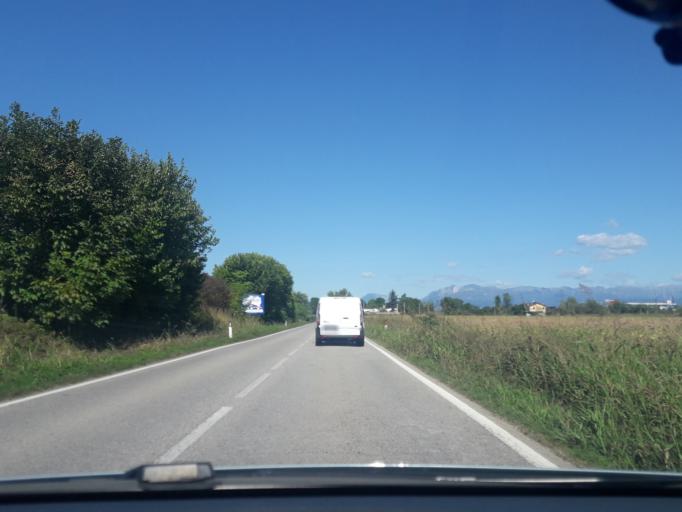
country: IT
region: Friuli Venezia Giulia
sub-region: Provincia di Udine
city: Basaldella
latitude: 46.0228
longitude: 13.2397
